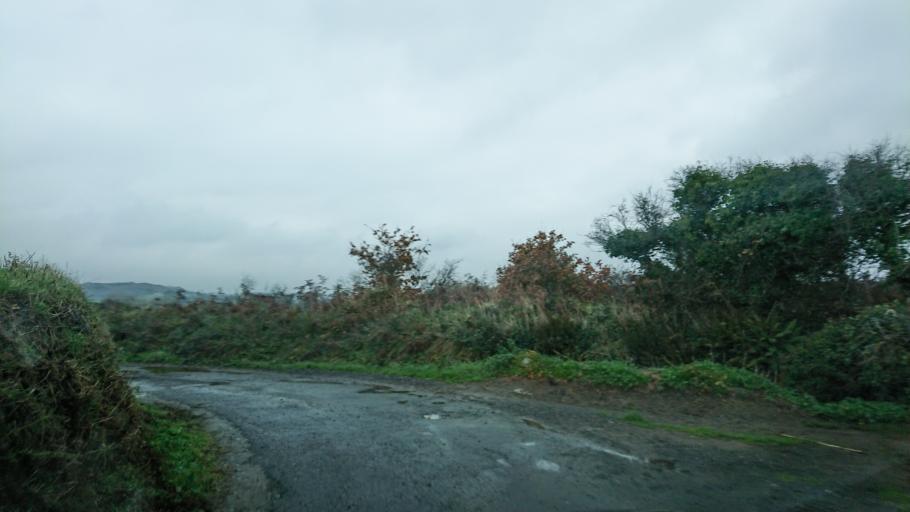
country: IE
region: Munster
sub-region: Waterford
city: Tra Mhor
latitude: 52.1986
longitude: -7.1501
